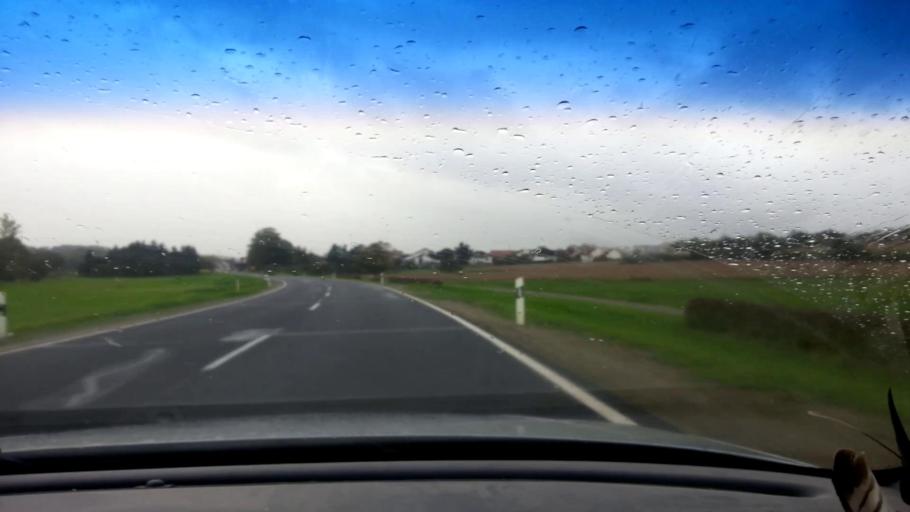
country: DE
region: Bavaria
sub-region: Upper Franconia
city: Stegaurach
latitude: 49.8699
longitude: 10.8243
